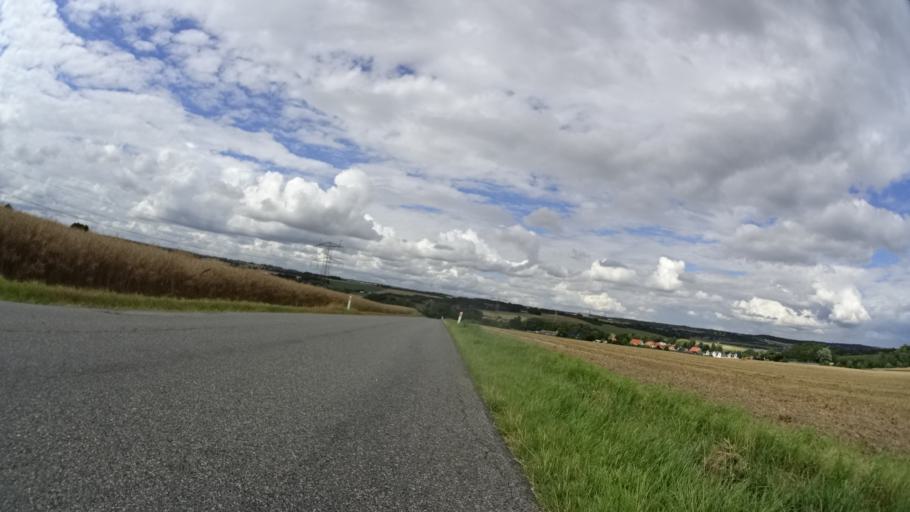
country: DK
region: Central Jutland
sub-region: Arhus Kommune
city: Kolt
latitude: 56.1269
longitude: 10.0424
